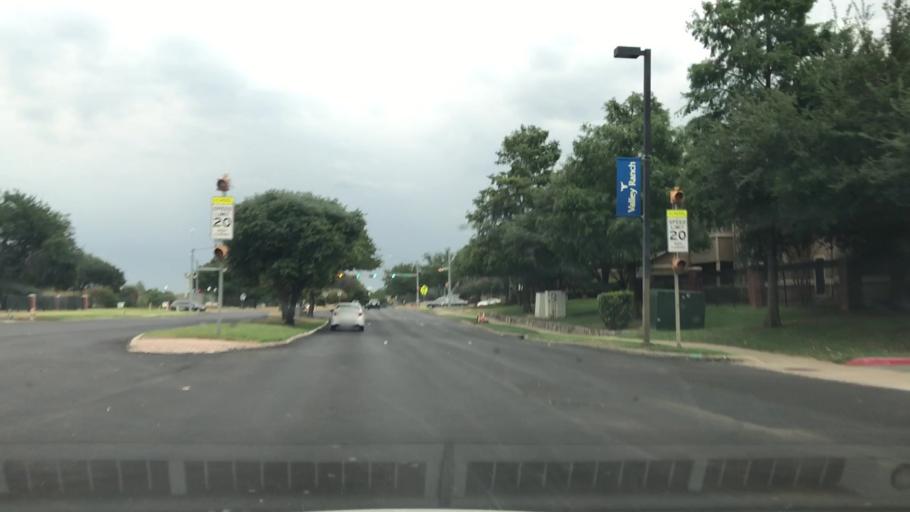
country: US
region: Texas
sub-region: Dallas County
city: Coppell
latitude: 32.9474
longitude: -96.9557
